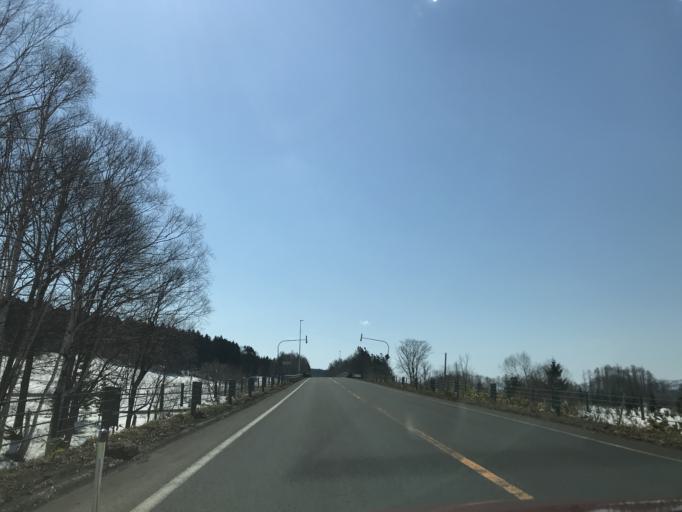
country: JP
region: Hokkaido
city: Nayoro
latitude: 44.7217
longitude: 142.2700
